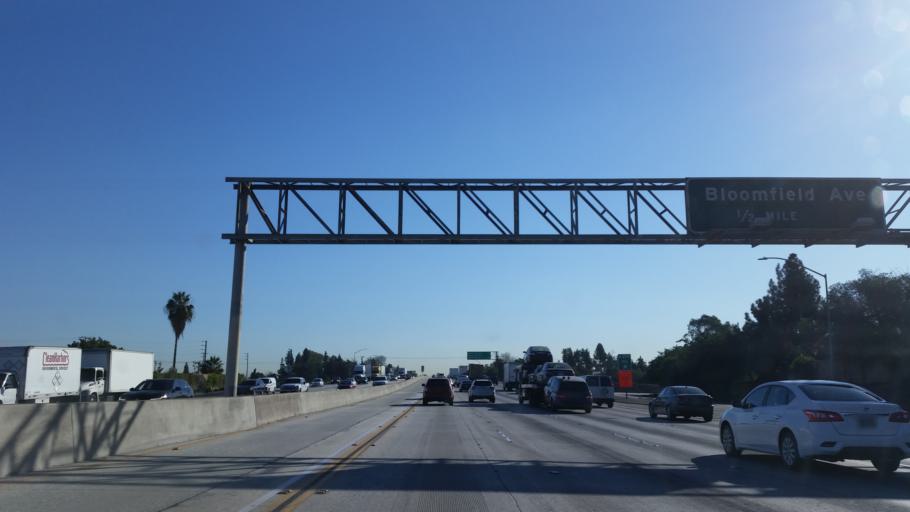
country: US
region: California
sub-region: Los Angeles County
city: Artesia
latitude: 33.8764
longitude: -118.0768
